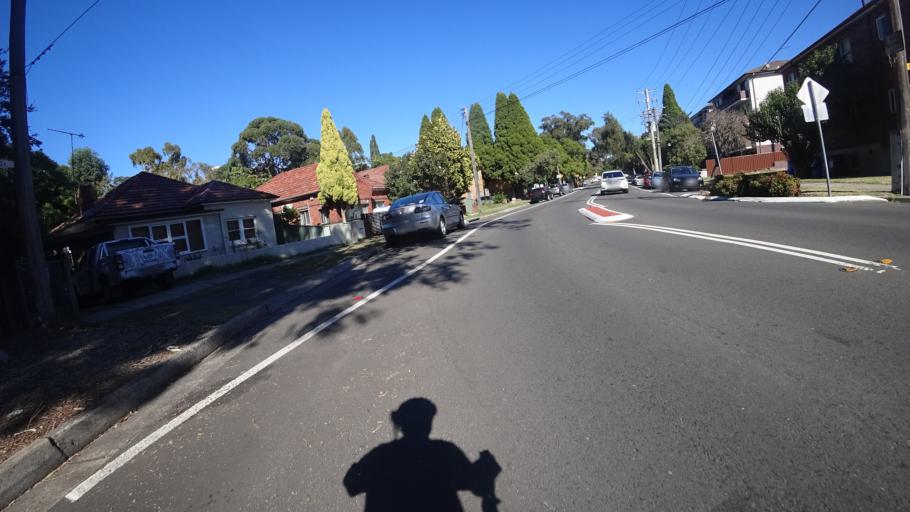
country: AU
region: New South Wales
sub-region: Kogarah
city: Beverly Park
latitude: -33.9599
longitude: 151.1320
